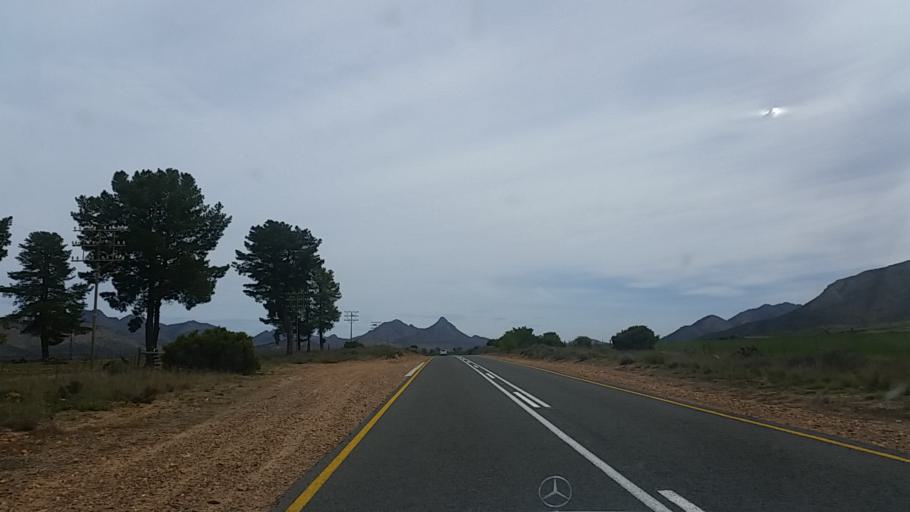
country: ZA
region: Western Cape
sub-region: Eden District Municipality
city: George
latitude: -33.8197
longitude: 22.4977
